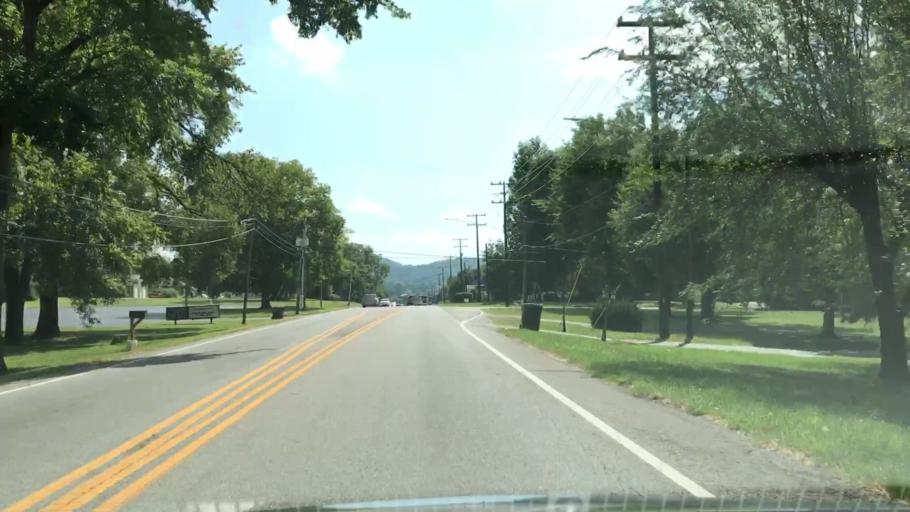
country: US
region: Tennessee
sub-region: Trousdale County
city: Hartsville
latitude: 36.3880
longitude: -86.1404
